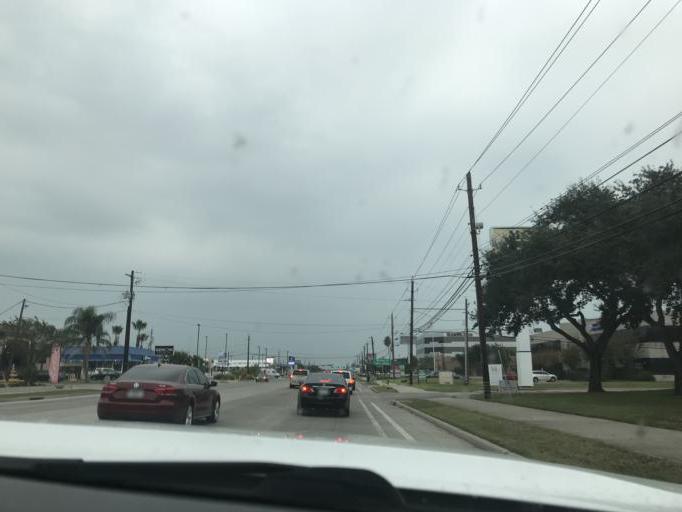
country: US
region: Texas
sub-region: Nueces County
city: Corpus Christi
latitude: 27.7019
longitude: -97.3735
